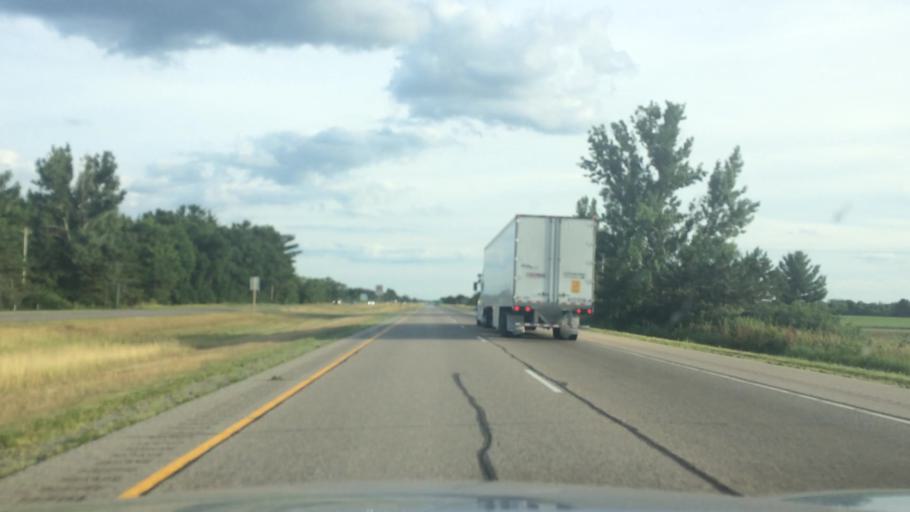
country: US
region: Wisconsin
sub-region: Portage County
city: Plover
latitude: 44.2453
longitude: -89.5243
